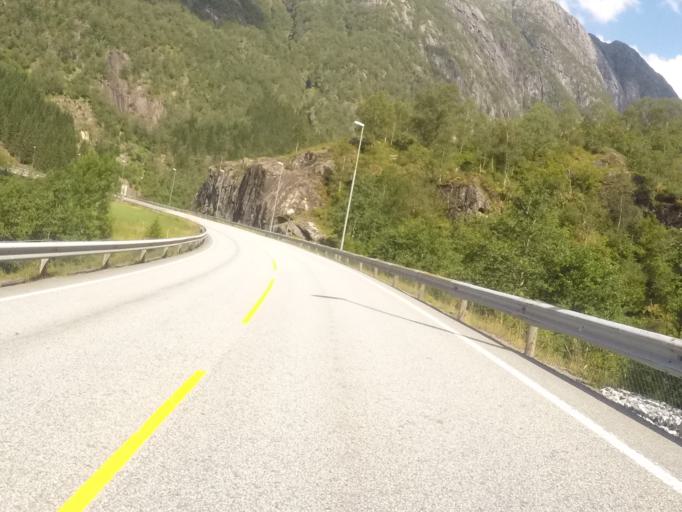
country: NO
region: Hordaland
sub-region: Masfjorden
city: Masfjorden
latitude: 60.9154
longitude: 5.5317
